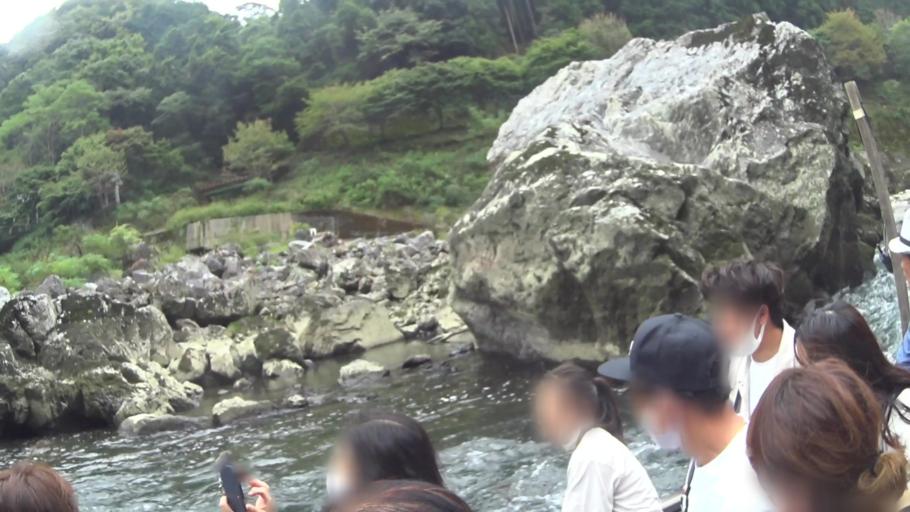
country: JP
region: Kyoto
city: Kameoka
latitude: 35.0184
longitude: 135.6356
